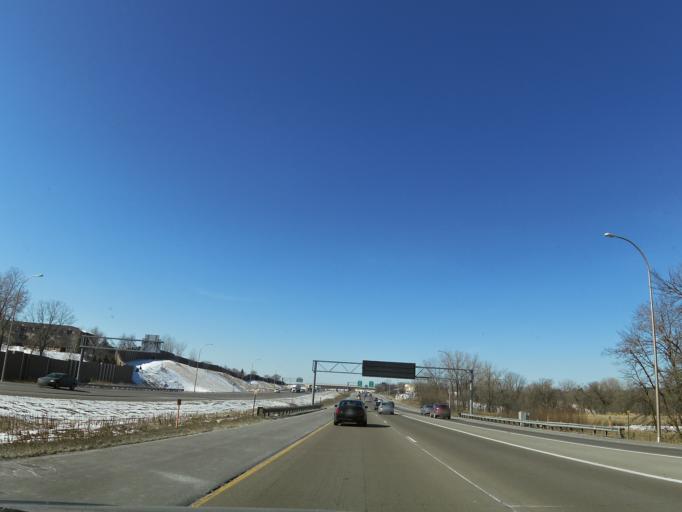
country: US
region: Minnesota
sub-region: Ramsey County
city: Vadnais Heights
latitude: 45.0377
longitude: -93.0481
